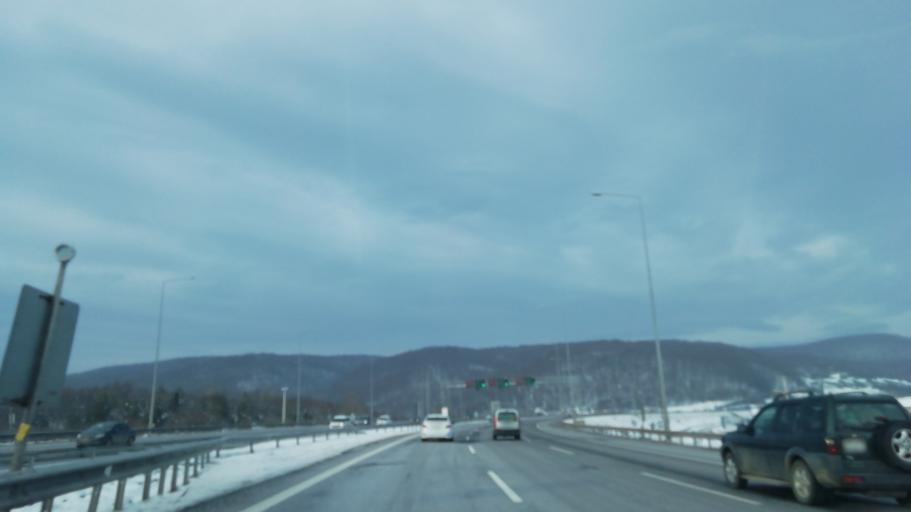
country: TR
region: Duzce
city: Kaynasli
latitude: 40.7297
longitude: 31.4443
